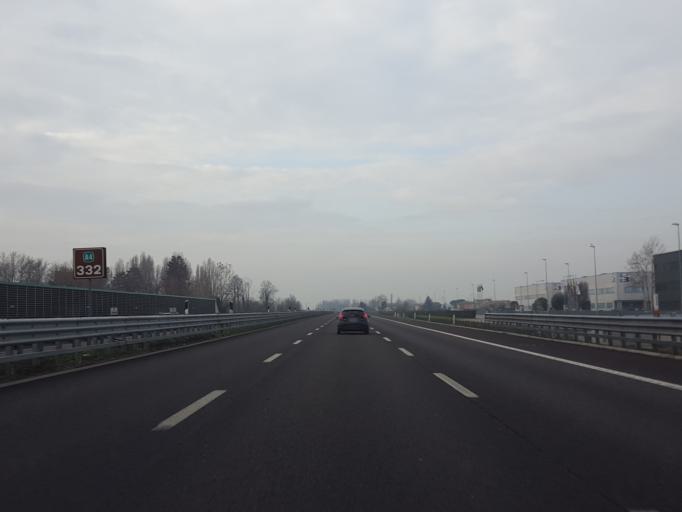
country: IT
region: Veneto
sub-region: Provincia di Padova
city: Ronchi di Campanile
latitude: 45.4607
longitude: 11.7767
